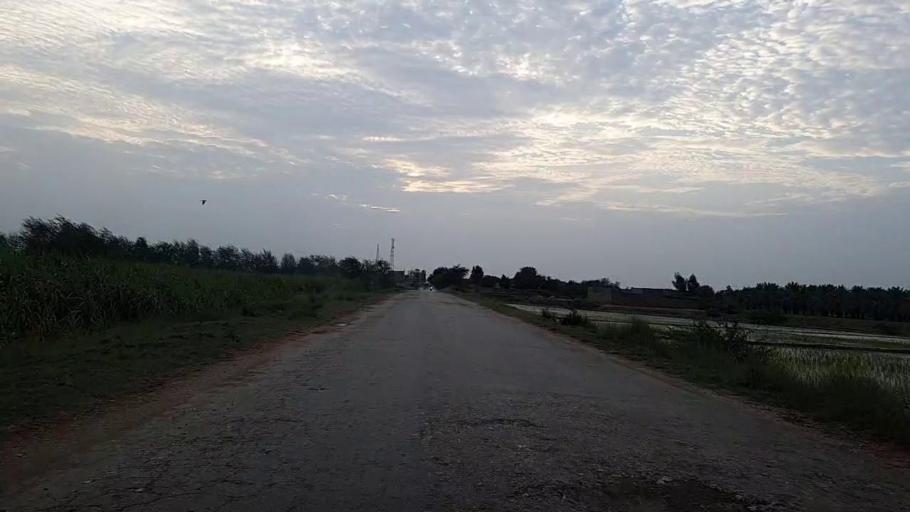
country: PK
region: Sindh
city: Naushahro Firoz
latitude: 26.8080
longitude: 68.2043
